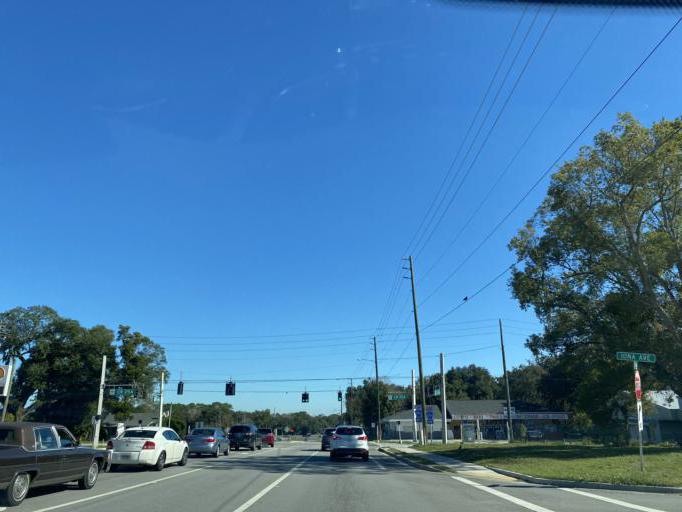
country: US
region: Florida
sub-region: Lake County
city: Fruitland Park
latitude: 28.8613
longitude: -81.9075
